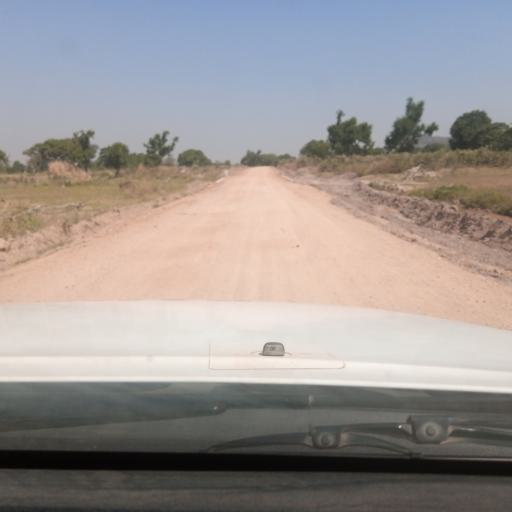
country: NG
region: Adamawa
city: Yola
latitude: 9.0522
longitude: 12.3874
